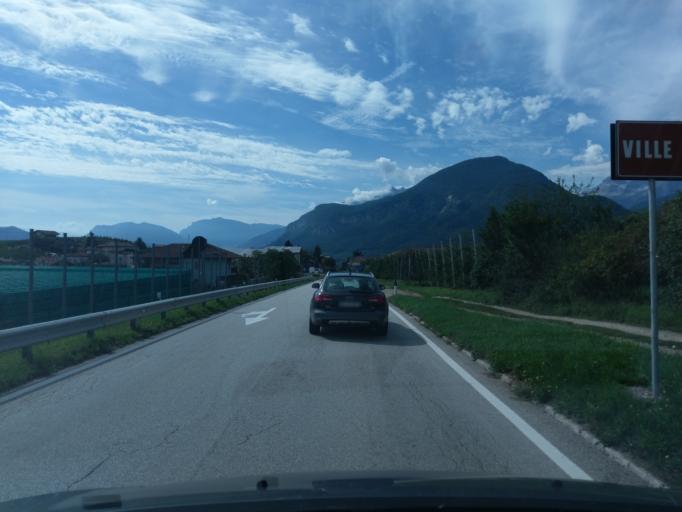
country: IT
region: Trentino-Alto Adige
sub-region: Provincia di Trento
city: Tuenno
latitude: 46.3369
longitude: 11.0269
